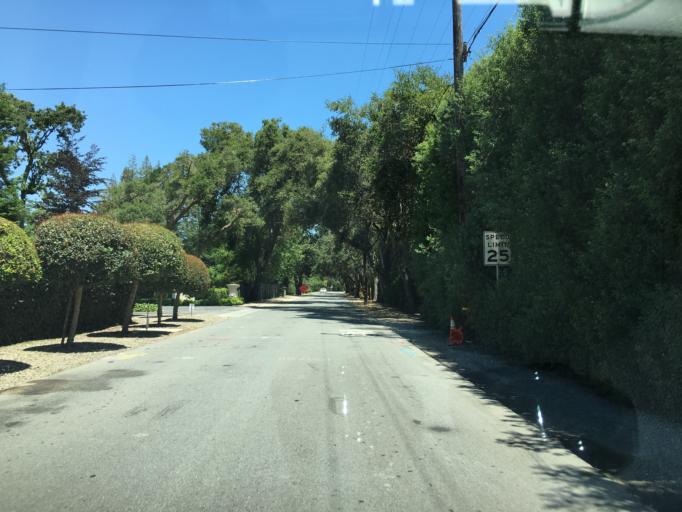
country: US
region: California
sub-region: San Mateo County
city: West Menlo Park
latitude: 37.4448
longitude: -122.2026
